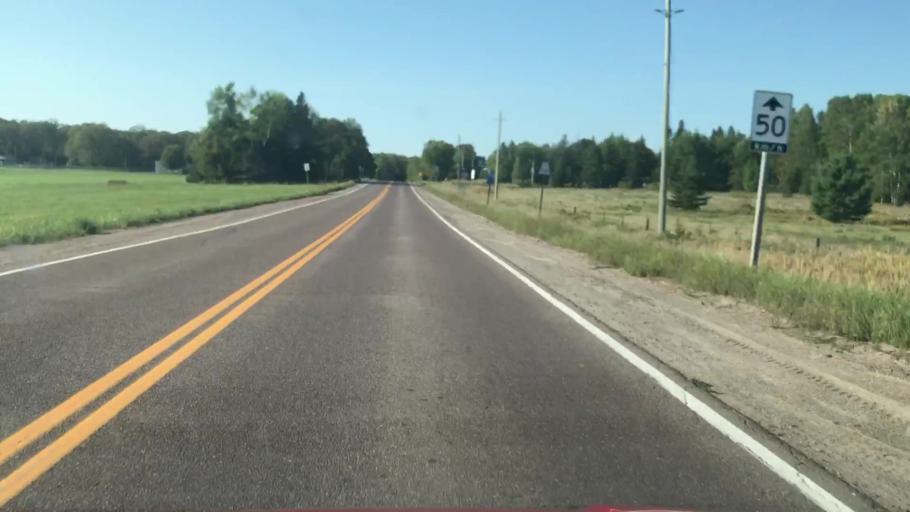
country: US
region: Michigan
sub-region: Chippewa County
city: Sault Ste. Marie
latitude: 46.2764
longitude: -84.0282
